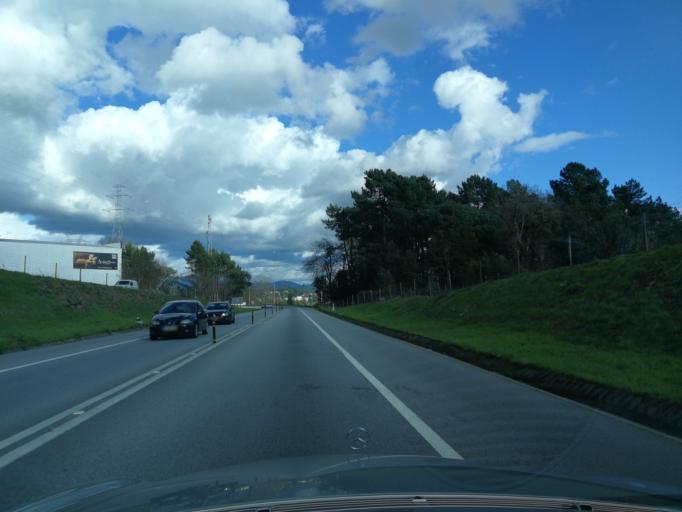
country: PT
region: Braga
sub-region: Vila Verde
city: Vila Verde
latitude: 41.6165
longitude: -8.4383
